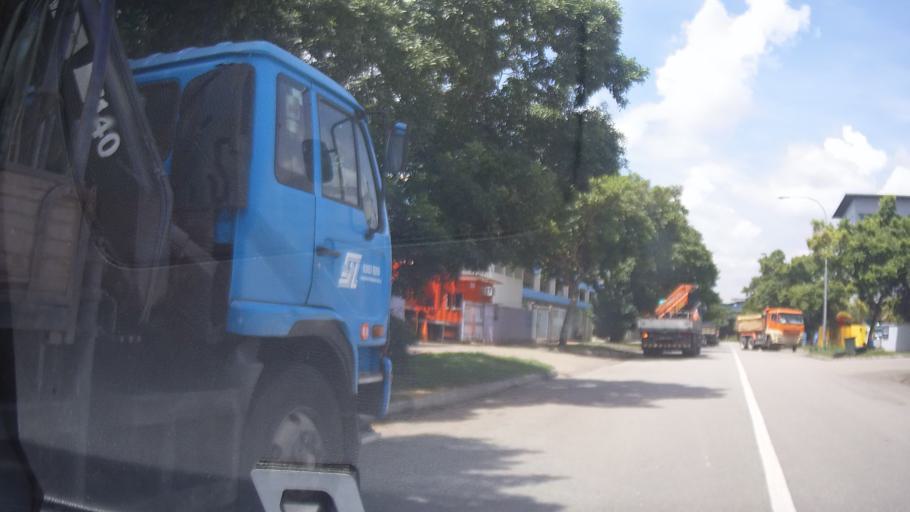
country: MY
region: Johor
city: Johor Bahru
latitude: 1.4348
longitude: 103.7460
